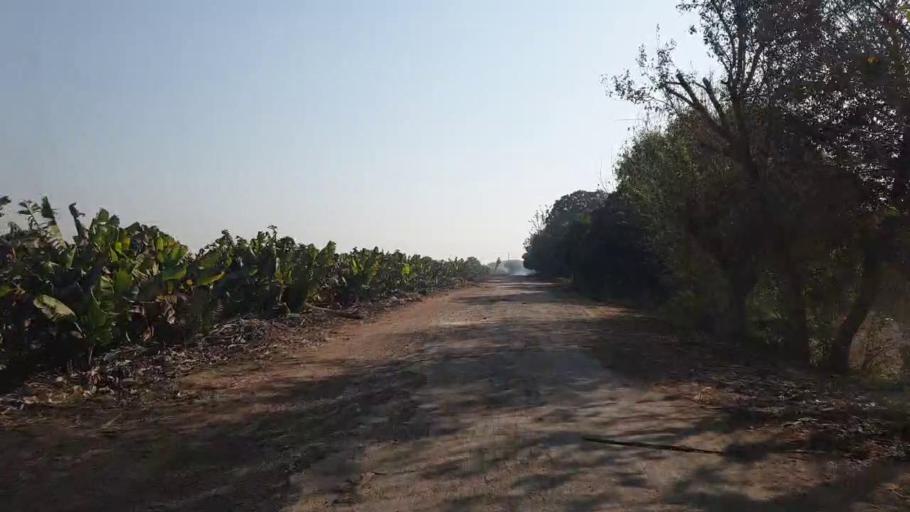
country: PK
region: Sindh
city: Tando Allahyar
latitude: 25.3685
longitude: 68.6659
